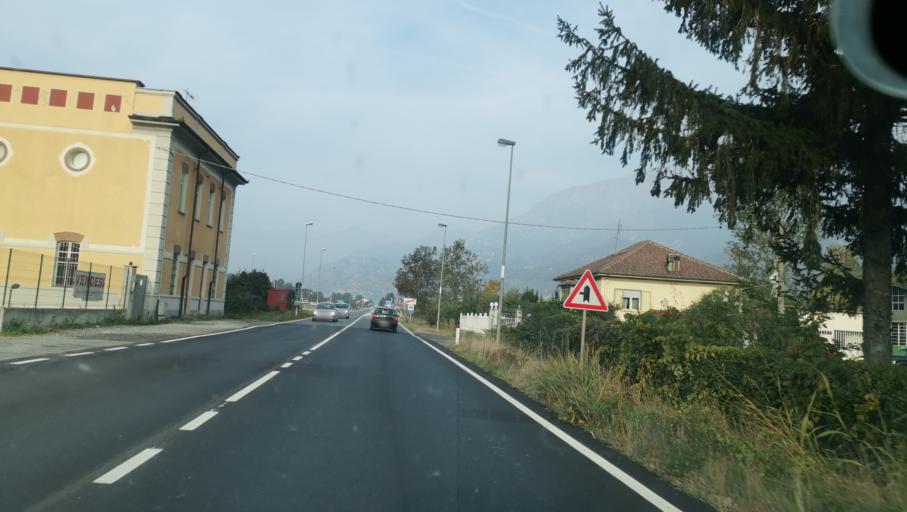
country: IT
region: Piedmont
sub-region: Provincia di Torino
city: Borgone Susa
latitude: 45.1255
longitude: 7.2235
